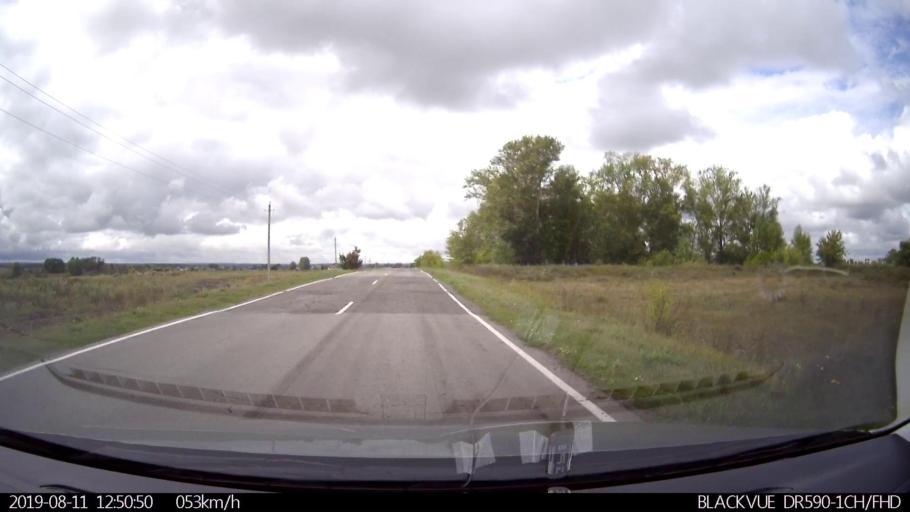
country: RU
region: Ulyanovsk
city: Ignatovka
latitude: 53.8754
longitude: 47.6680
